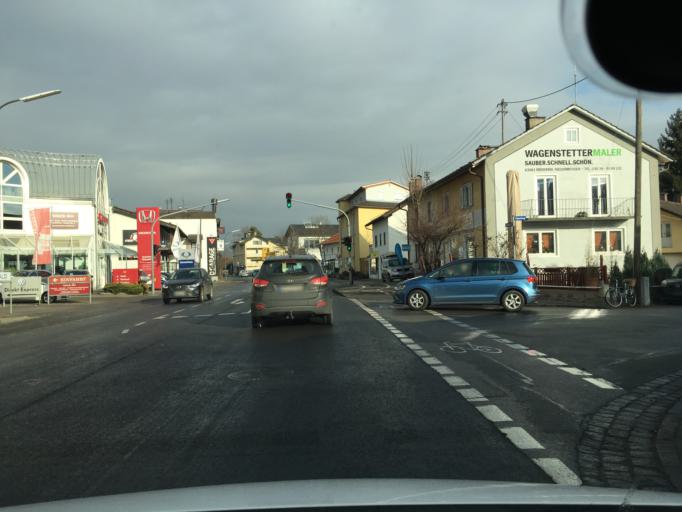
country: DE
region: Bavaria
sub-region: Upper Bavaria
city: Rosenheim
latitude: 47.8425
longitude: 12.1232
